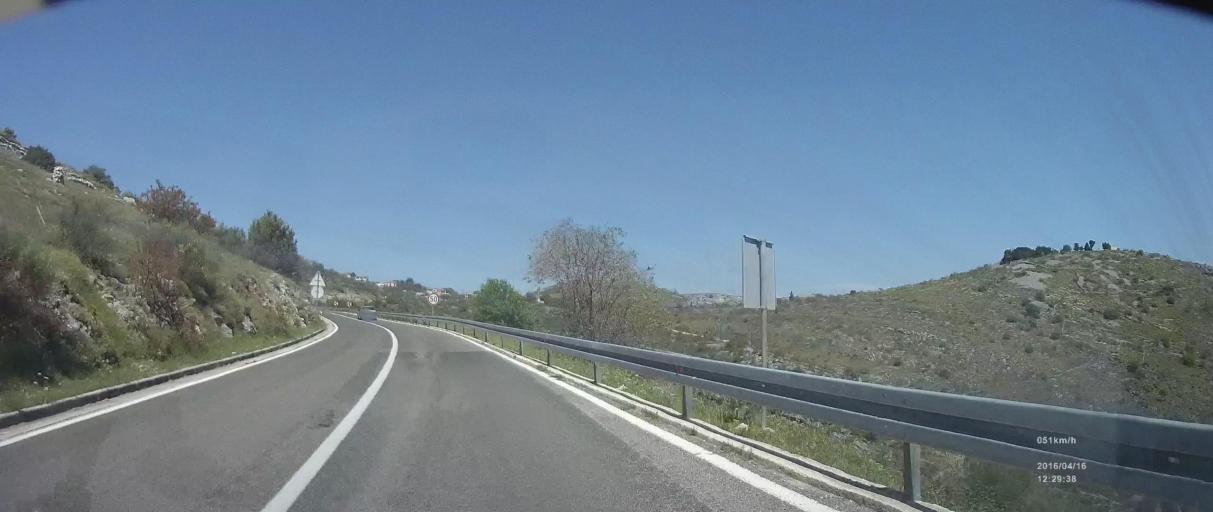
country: HR
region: Splitsko-Dalmatinska
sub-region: Grad Trogir
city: Trogir
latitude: 43.5253
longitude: 16.2199
